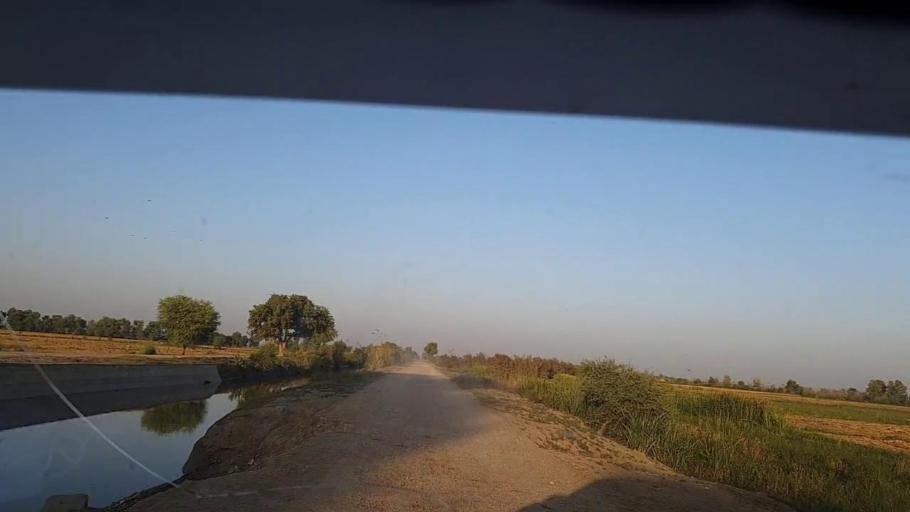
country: PK
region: Sindh
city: Ratodero
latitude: 27.8847
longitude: 68.2114
